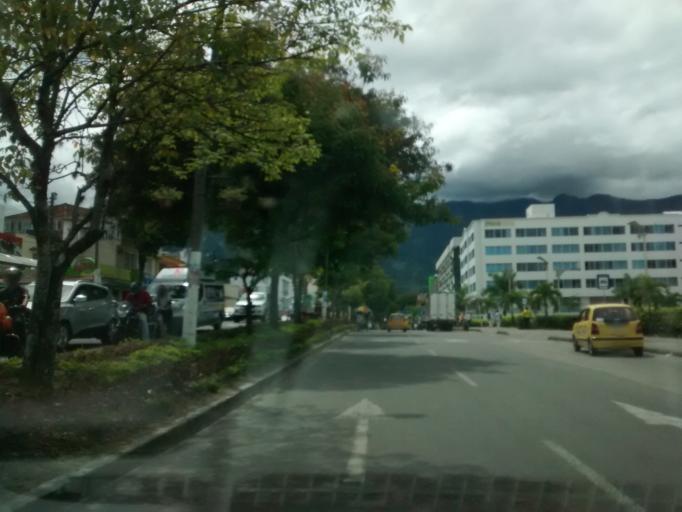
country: CO
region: Tolima
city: Ibague
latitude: 4.4368
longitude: -75.2032
